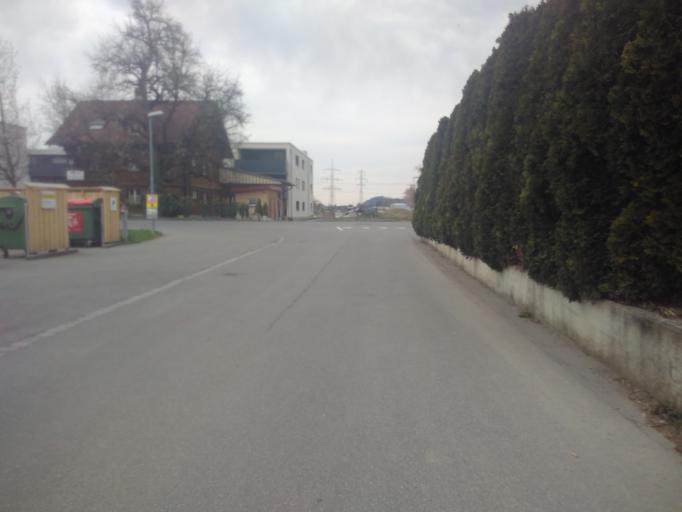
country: AT
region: Vorarlberg
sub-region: Politischer Bezirk Feldkirch
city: Rankweil
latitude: 47.2666
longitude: 9.6186
